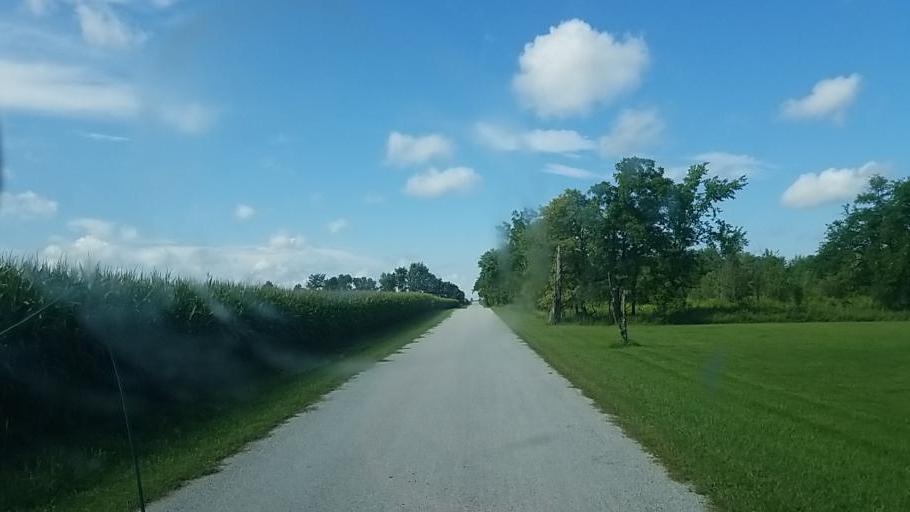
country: US
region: Ohio
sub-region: Hardin County
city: Kenton
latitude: 40.6736
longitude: -83.5476
